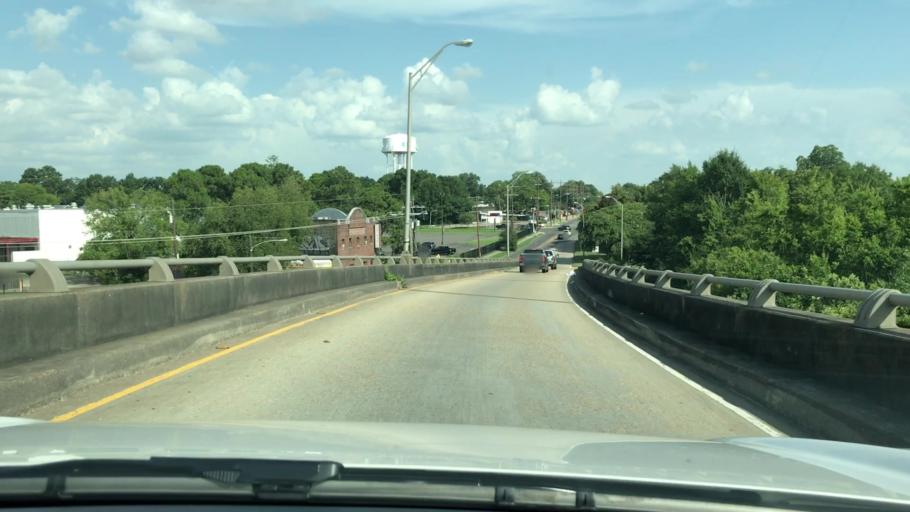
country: US
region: Louisiana
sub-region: West Baton Rouge Parish
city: Port Allen
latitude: 30.4381
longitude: -91.1867
